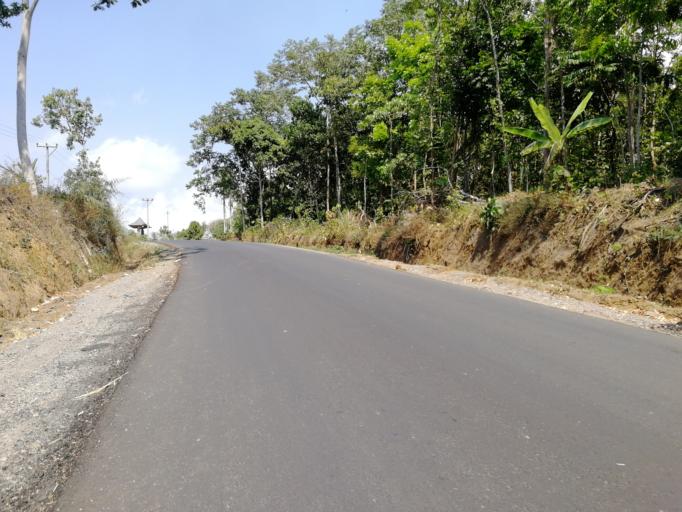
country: ID
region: West Nusa Tenggara
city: Lelongken
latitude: -8.3196
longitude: 116.4914
